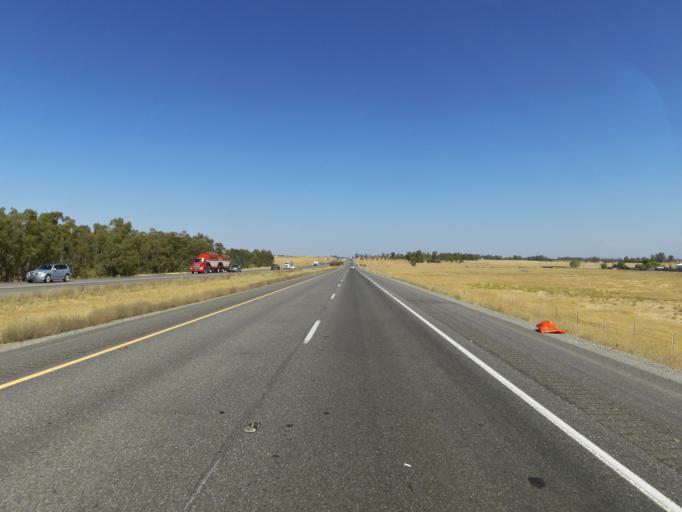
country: US
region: California
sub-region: Tehama County
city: Corning
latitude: 39.8520
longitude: -122.1999
